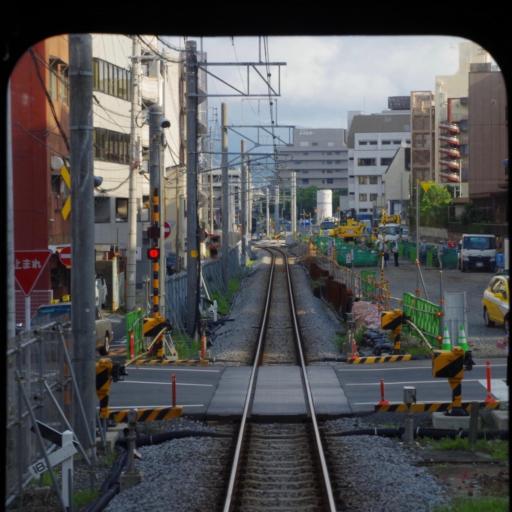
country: JP
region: Nagasaki
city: Nagasaki-shi
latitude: 32.7696
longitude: 129.8627
